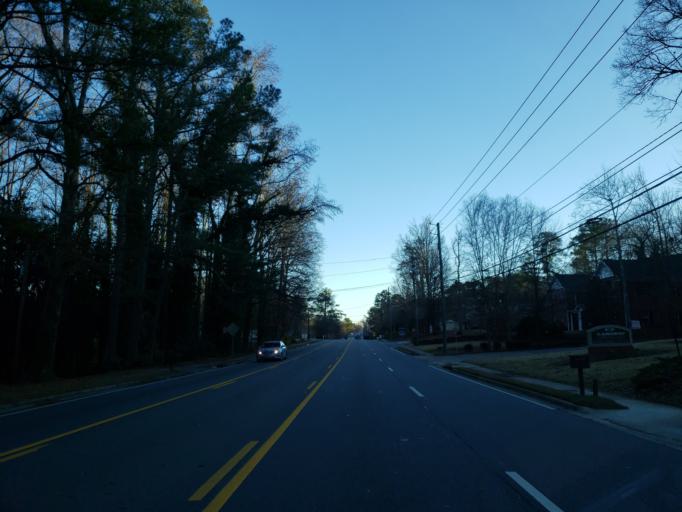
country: US
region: Georgia
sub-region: Fulton County
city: Alpharetta
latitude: 34.0864
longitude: -84.2952
